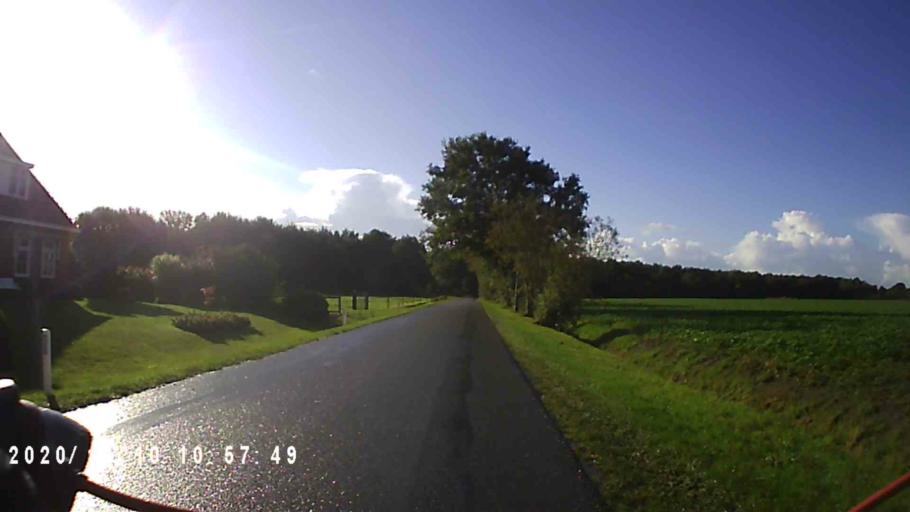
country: NL
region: Friesland
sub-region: Gemeente Achtkarspelen
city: Surhuisterveen
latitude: 53.1470
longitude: 6.2063
